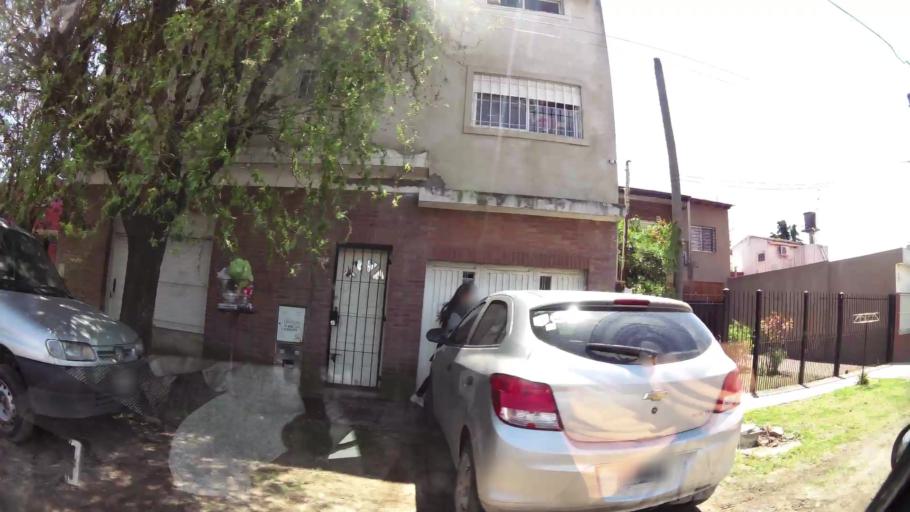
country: AR
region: Buenos Aires
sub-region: Partido de Quilmes
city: Quilmes
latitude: -34.7884
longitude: -58.2709
